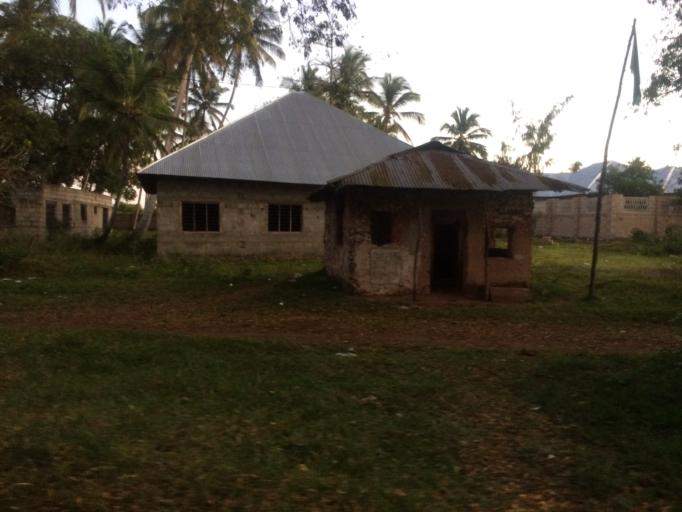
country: TZ
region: Zanzibar Central/South
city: Koani
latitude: -6.2017
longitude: 39.3177
